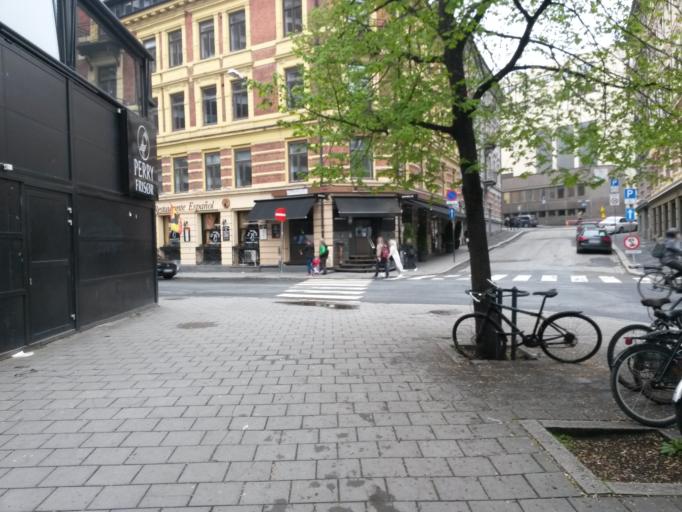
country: NO
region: Oslo
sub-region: Oslo
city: Oslo
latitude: 59.9188
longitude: 10.7346
